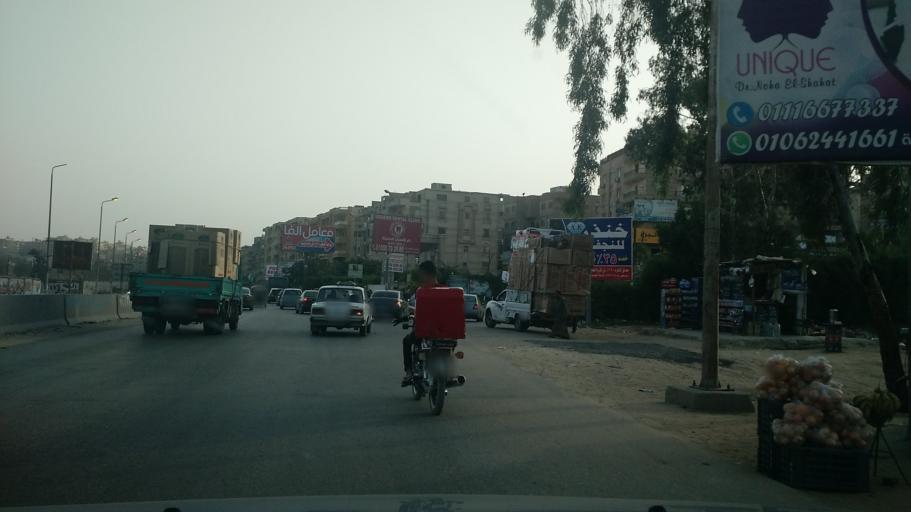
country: EG
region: Al Jizah
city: Al Jizah
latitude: 29.9782
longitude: 31.1129
